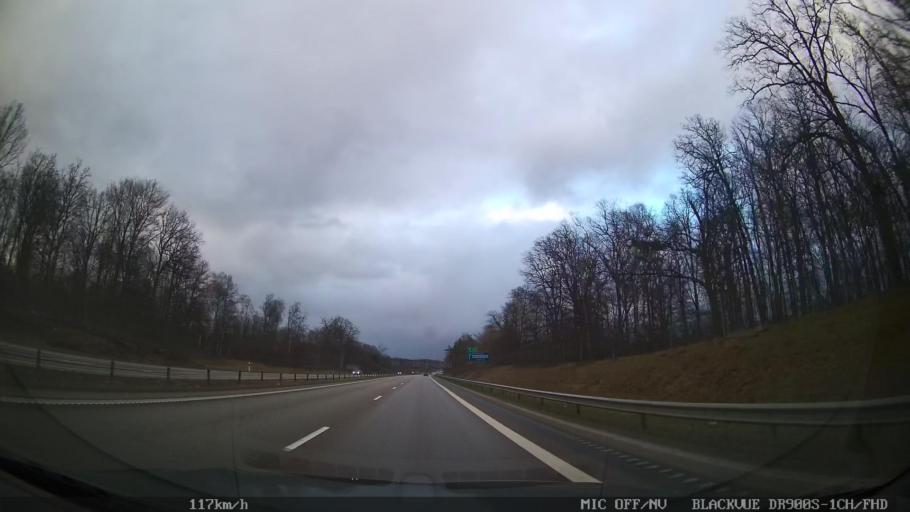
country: SE
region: Skane
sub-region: Astorps Kommun
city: Kvidinge
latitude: 56.2041
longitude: 13.0917
